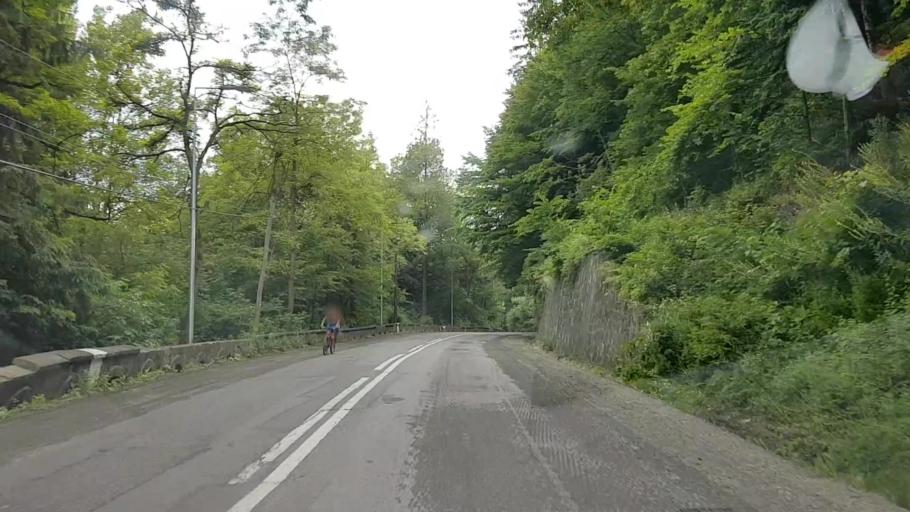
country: RO
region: Neamt
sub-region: Comuna Bicaz
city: Dodeni
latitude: 46.9332
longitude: 26.0976
